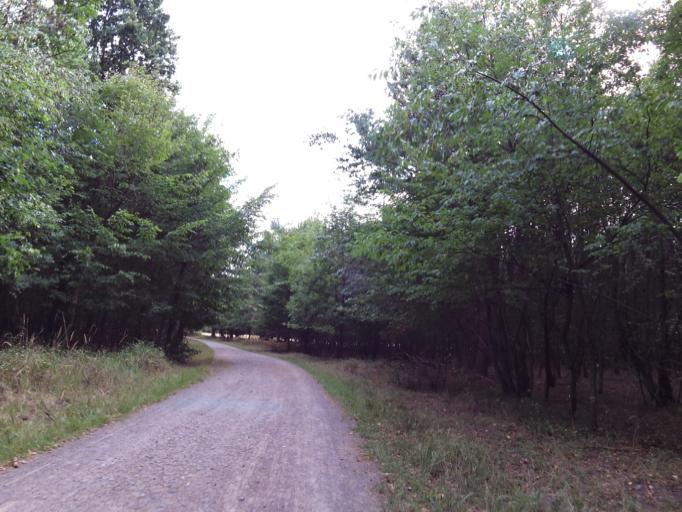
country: DE
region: Hesse
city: Morfelden-Walldorf
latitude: 49.9934
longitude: 8.5567
